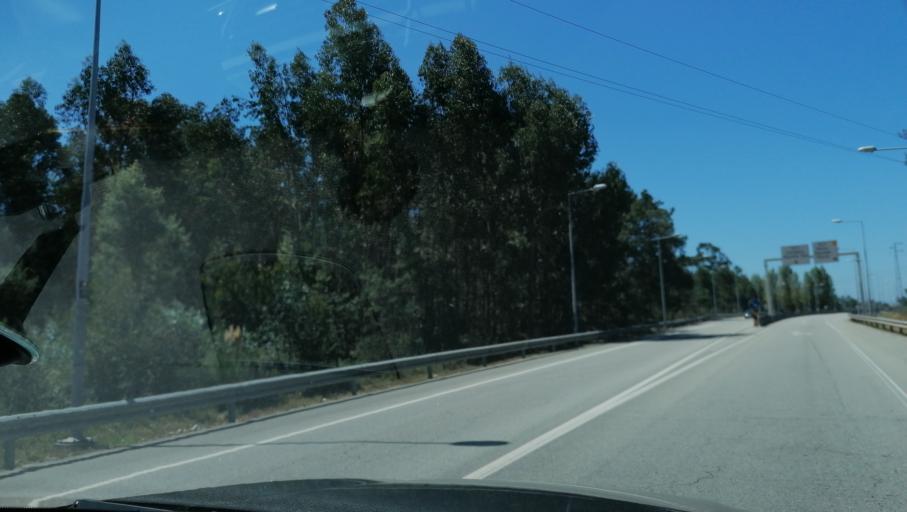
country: PT
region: Aveiro
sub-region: Agueda
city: Agueda
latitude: 40.5556
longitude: -8.4695
